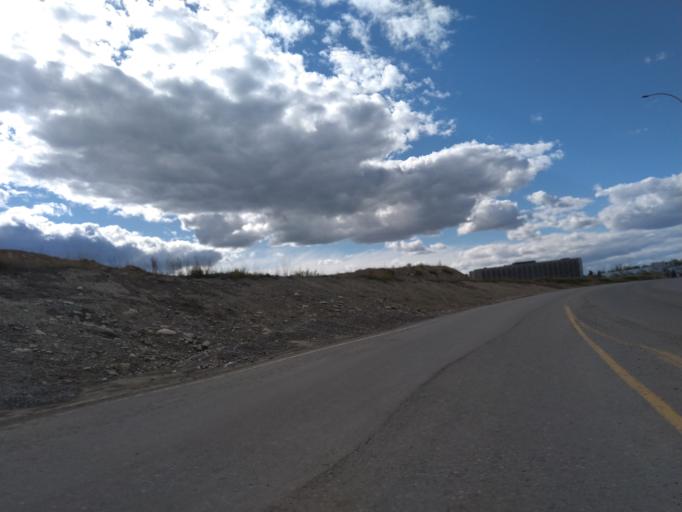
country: CA
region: Alberta
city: Calgary
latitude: 51.0038
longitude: -114.1440
